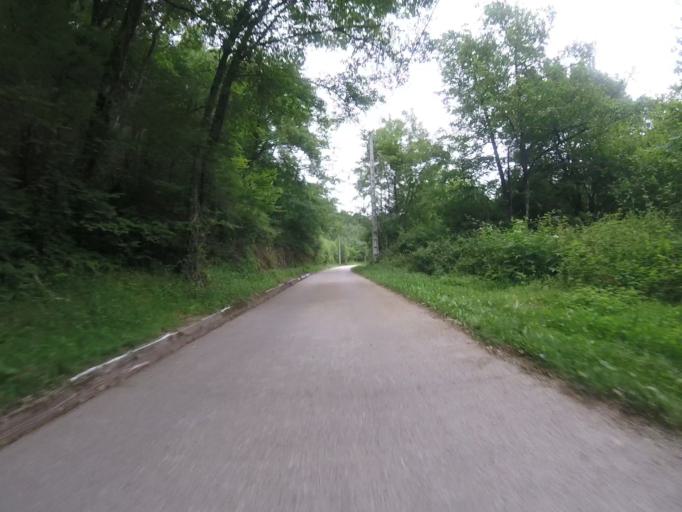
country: ES
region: Navarre
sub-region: Provincia de Navarra
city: Doneztebe
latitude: 43.1458
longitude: -1.6689
